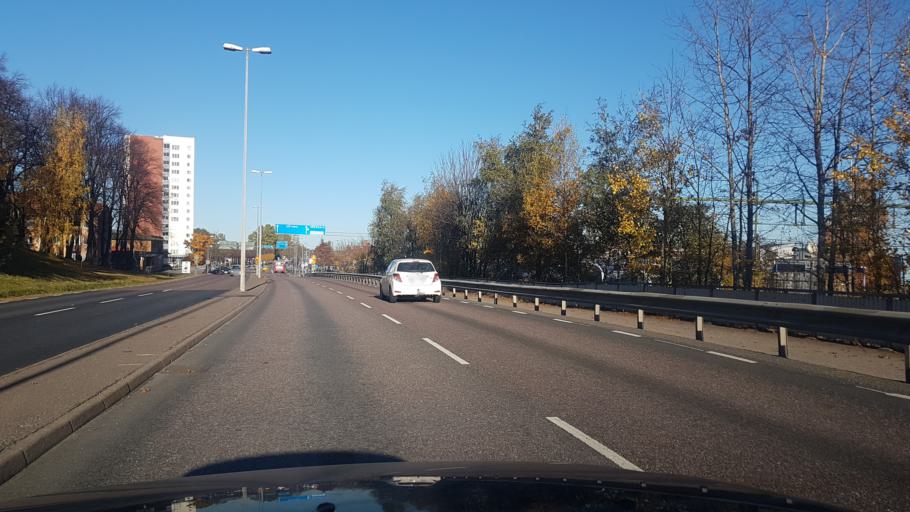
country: SE
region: Stockholm
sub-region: Sigtuna Kommun
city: Marsta
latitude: 59.6260
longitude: 17.8608
